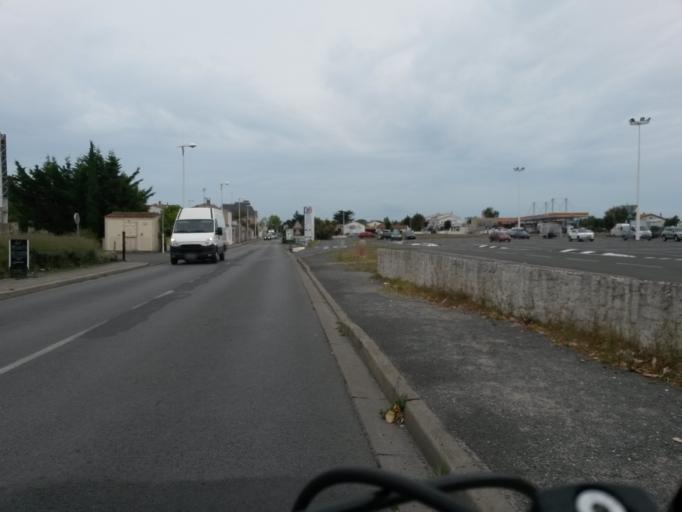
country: FR
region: Poitou-Charentes
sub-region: Departement de la Charente-Maritime
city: Dolus-d'Oleron
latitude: 45.9439
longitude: -1.3175
